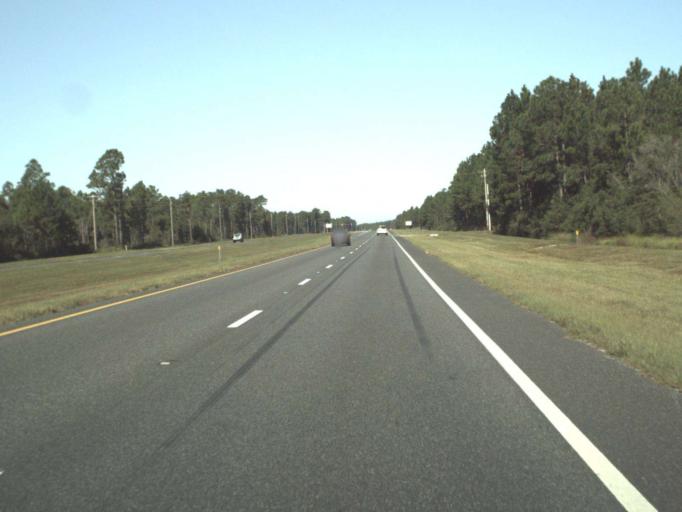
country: US
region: Florida
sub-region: Walton County
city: Seaside
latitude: 30.3363
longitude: -86.0627
